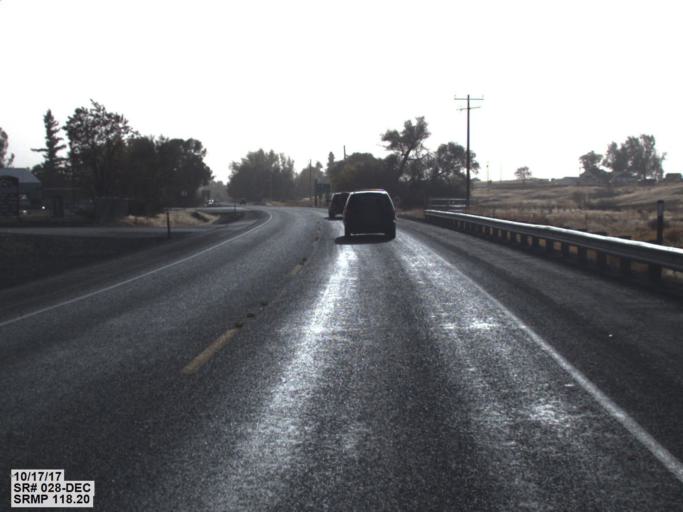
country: US
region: Washington
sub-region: Lincoln County
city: Davenport
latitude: 47.4866
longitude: -118.2538
